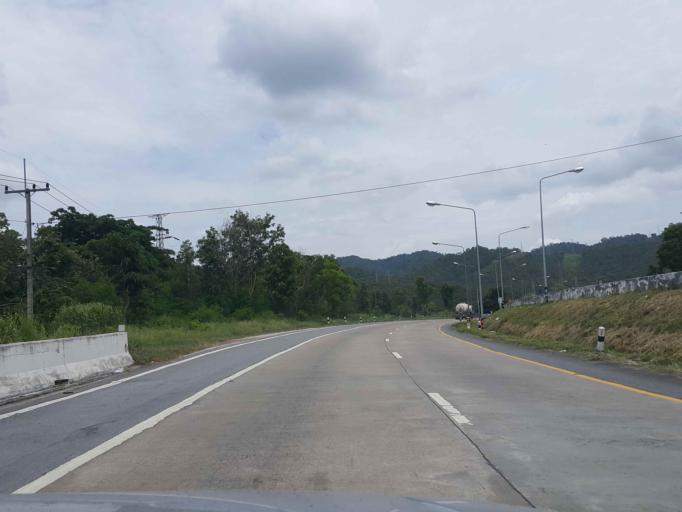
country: TH
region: Lamphun
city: Mae Tha
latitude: 18.4538
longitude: 99.1997
